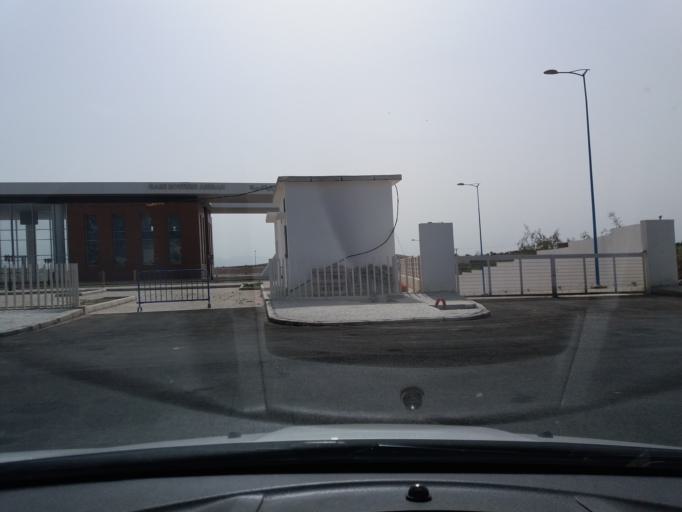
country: MA
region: Tanger-Tetouan
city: Asilah
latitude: 35.4608
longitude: -6.0289
